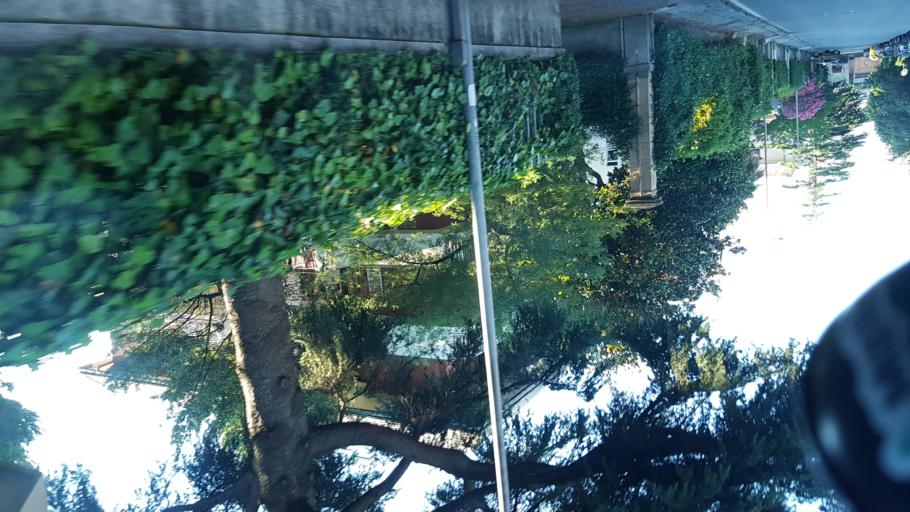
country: IT
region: Liguria
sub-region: Provincia di Genova
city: Genoa
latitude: 44.3993
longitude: 8.9677
